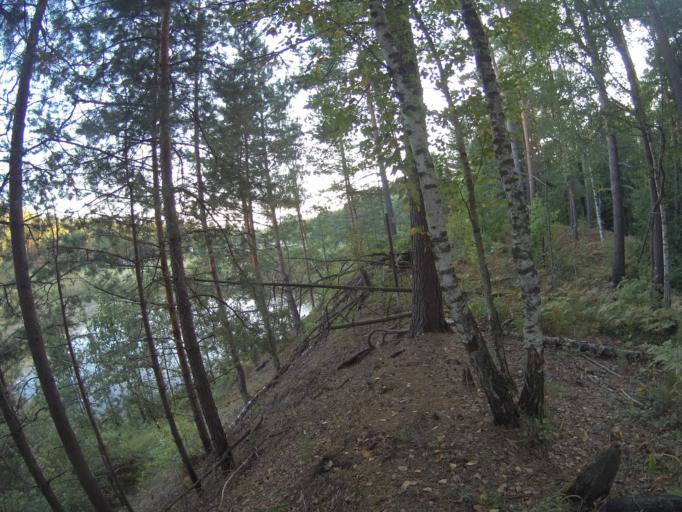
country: RU
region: Vladimir
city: Kommunar
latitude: 56.0478
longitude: 40.4338
